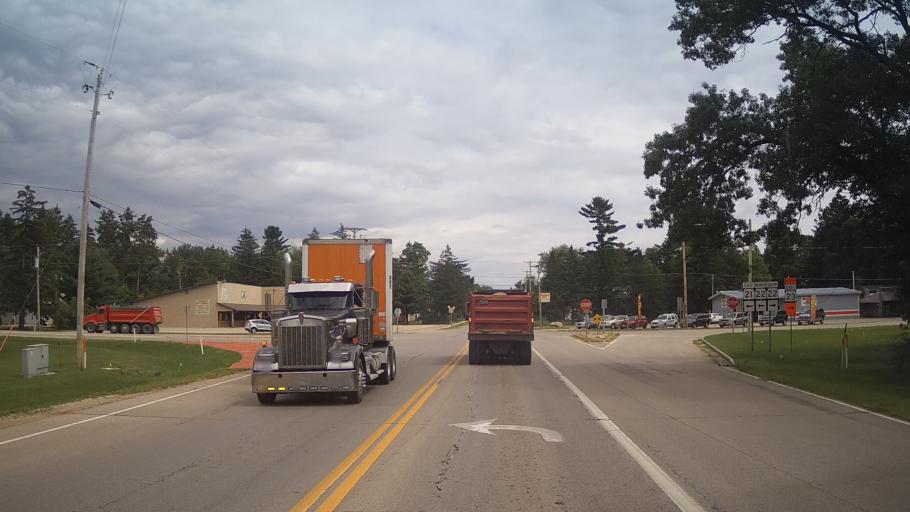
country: US
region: Wisconsin
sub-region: Waushara County
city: Wautoma
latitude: 44.0684
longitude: -89.2985
